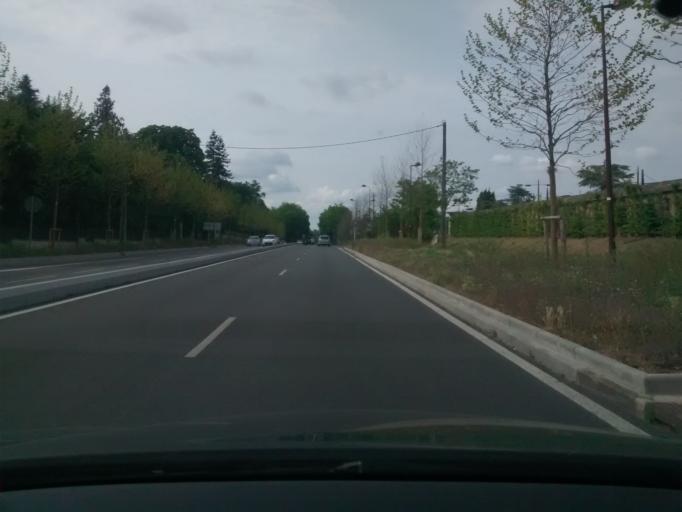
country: FR
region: Ile-de-France
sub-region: Departement des Yvelines
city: Le Chesnay
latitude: 48.8263
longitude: 2.1141
